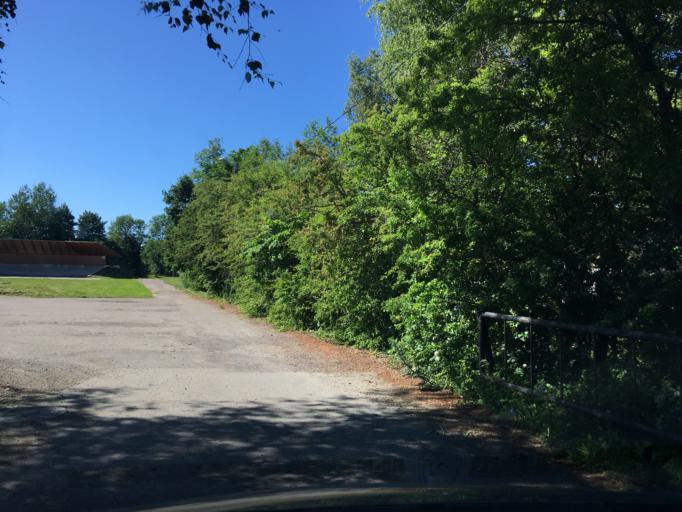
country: EE
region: Harju
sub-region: Raasiku vald
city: Raasiku
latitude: 59.1899
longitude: 25.1713
